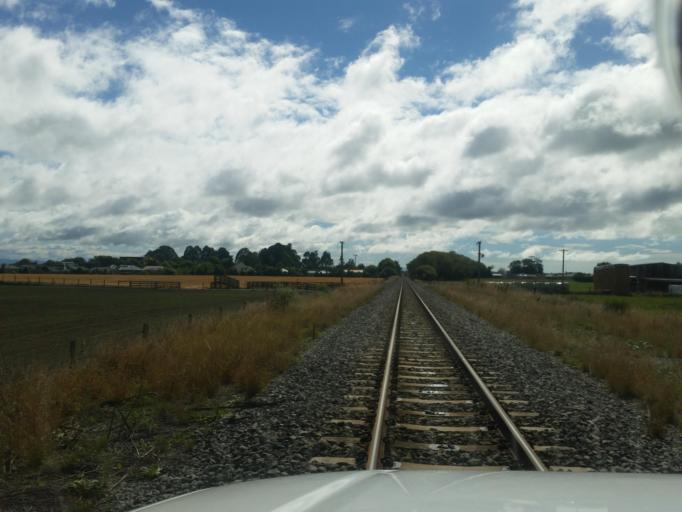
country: NZ
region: Canterbury
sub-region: Waimakariri District
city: Kaiapoi
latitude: -43.3998
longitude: 172.6529
